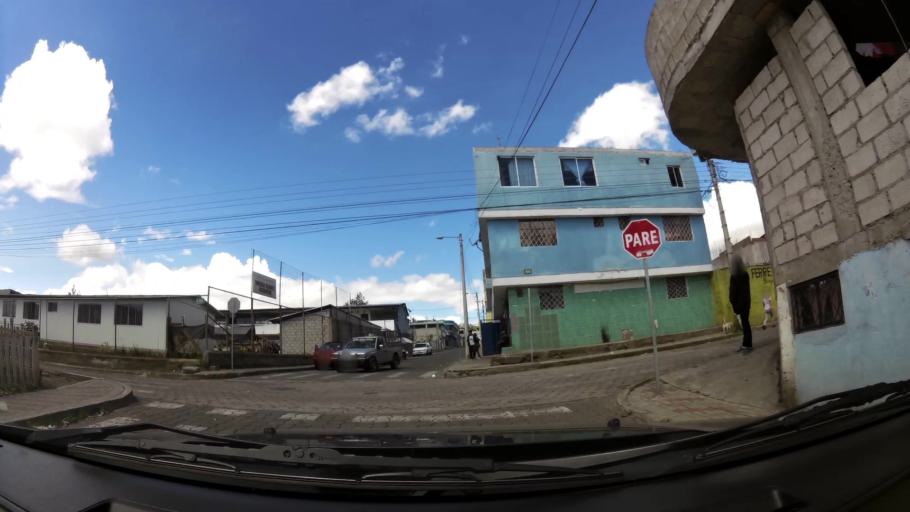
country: EC
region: Pichincha
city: Quito
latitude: -0.3238
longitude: -78.5624
